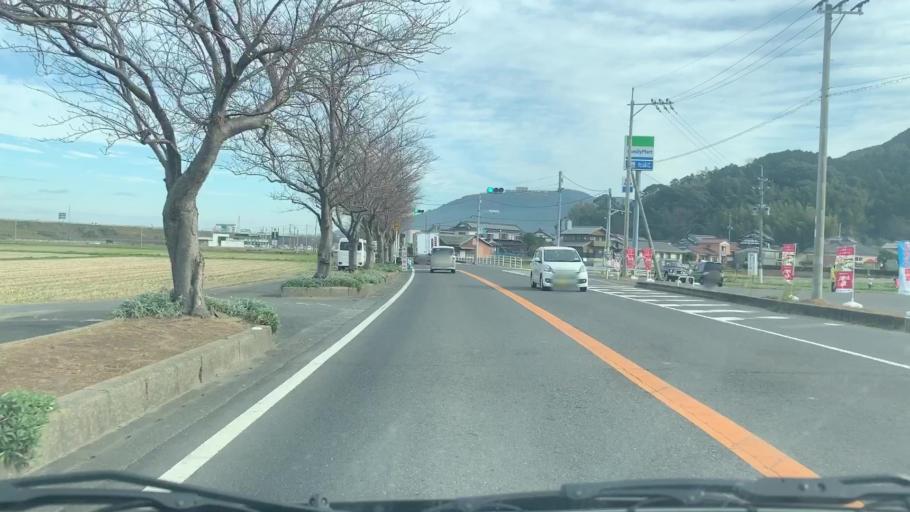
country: JP
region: Saga Prefecture
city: Karatsu
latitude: 33.4093
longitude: 129.9904
